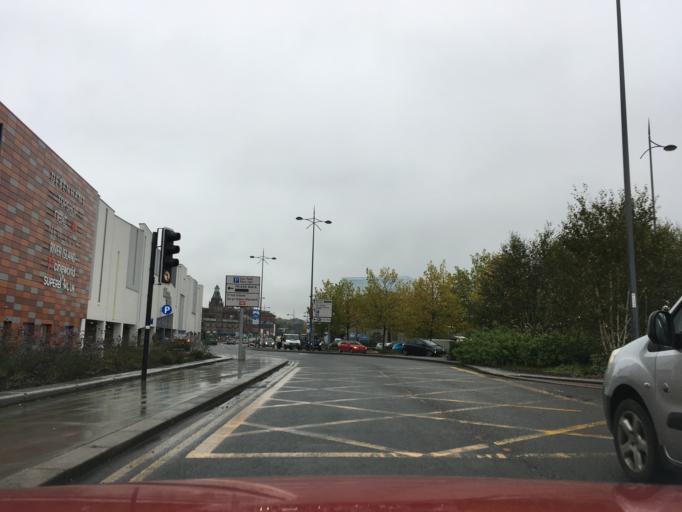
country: GB
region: Wales
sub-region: Newport
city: Newport
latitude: 51.5865
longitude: -2.9919
